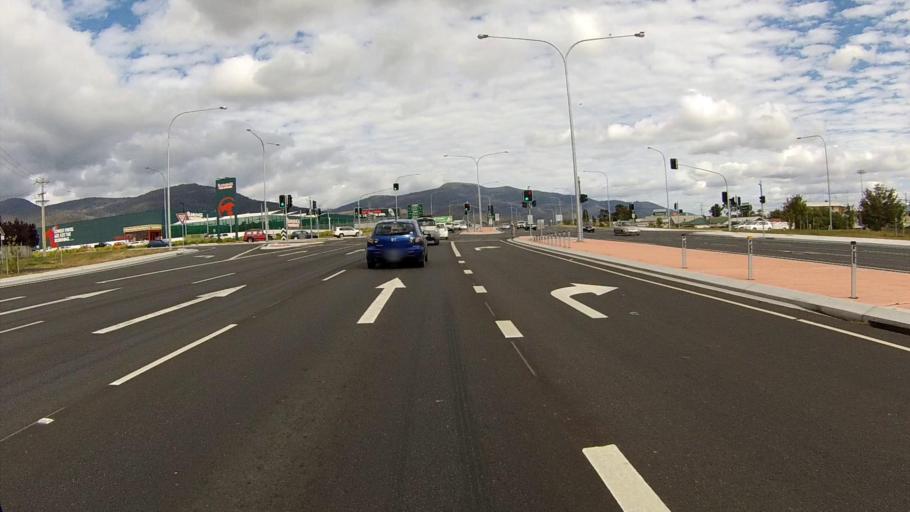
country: AU
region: Tasmania
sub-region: Glenorchy
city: Goodwood
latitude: -42.8301
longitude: 147.2900
